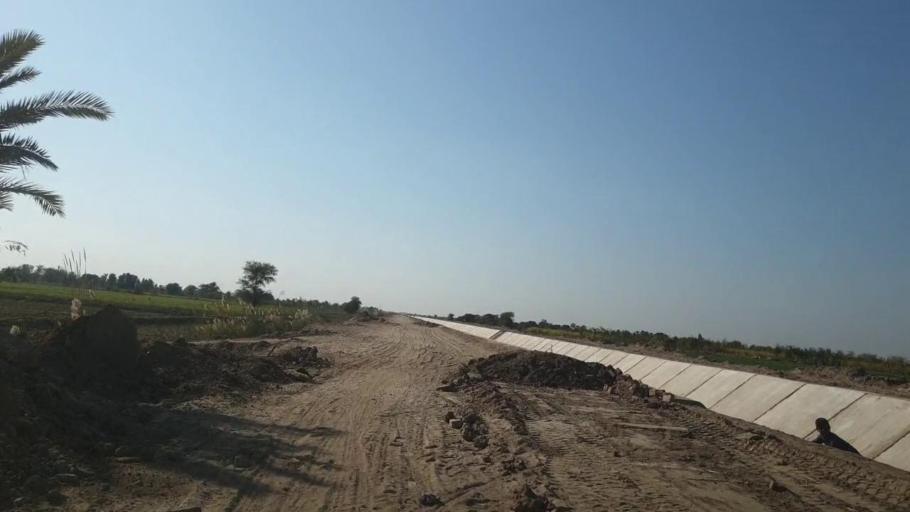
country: PK
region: Sindh
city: Mirpur Khas
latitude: 25.6450
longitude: 69.0559
